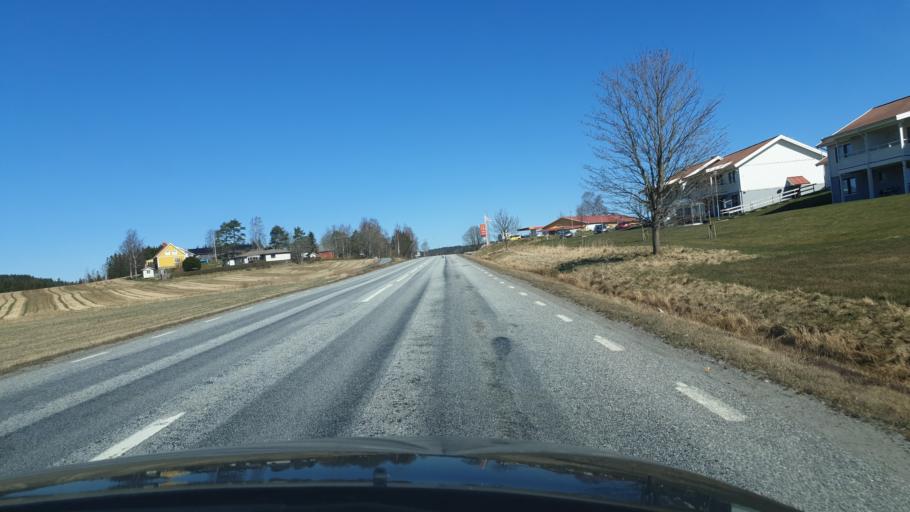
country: SE
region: Vaestra Goetaland
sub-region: Tanums Kommun
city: Tanumshede
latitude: 58.7742
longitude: 11.5586
